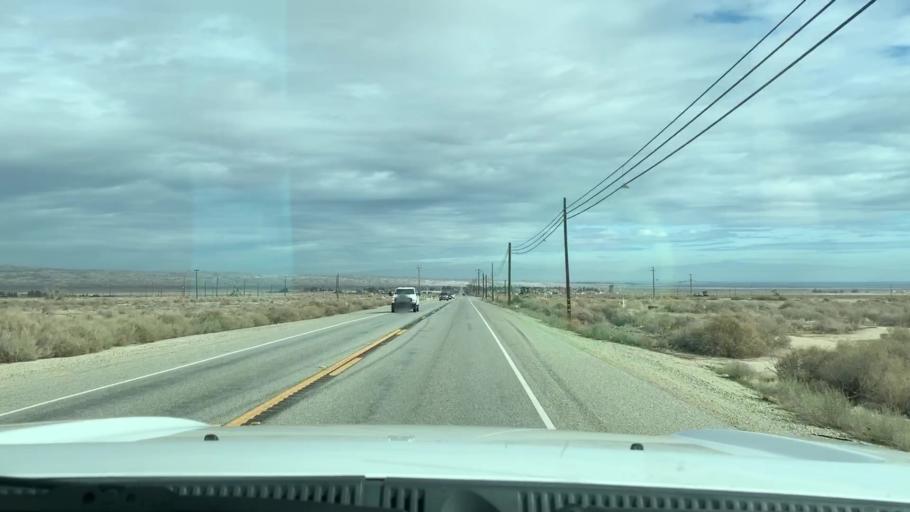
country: US
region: California
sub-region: Kern County
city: Ford City
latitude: 35.1919
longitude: -119.4316
